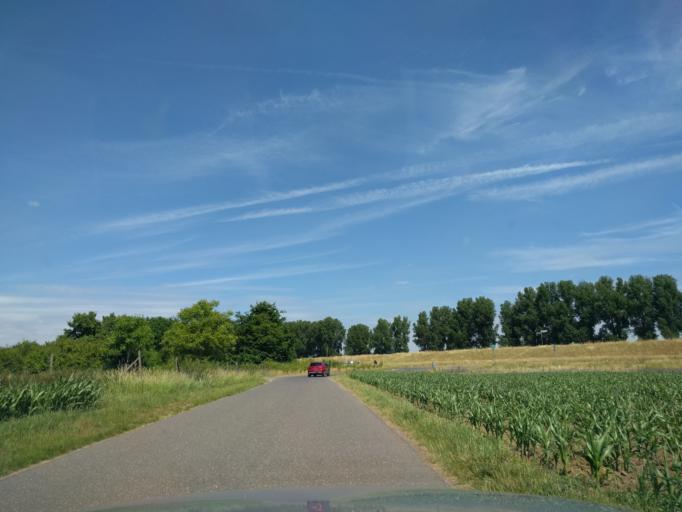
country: DE
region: North Rhine-Westphalia
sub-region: Regierungsbezirk Dusseldorf
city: Meerbusch
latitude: 51.2660
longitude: 6.6982
